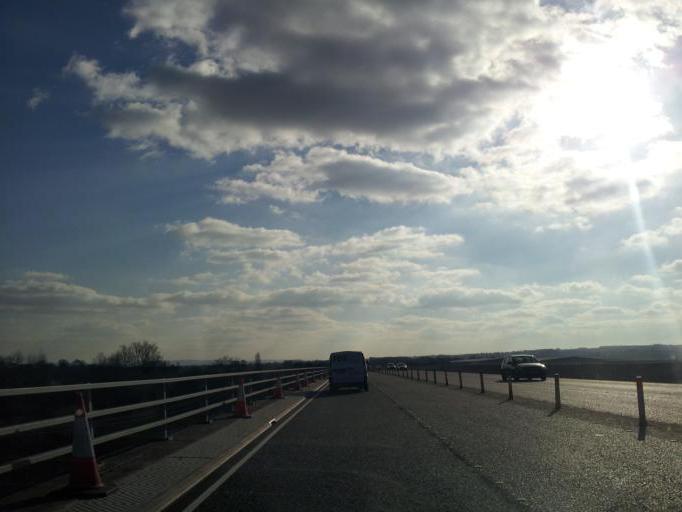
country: GB
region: England
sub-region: Somerset
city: Bridgwater
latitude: 51.1133
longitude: -2.9811
